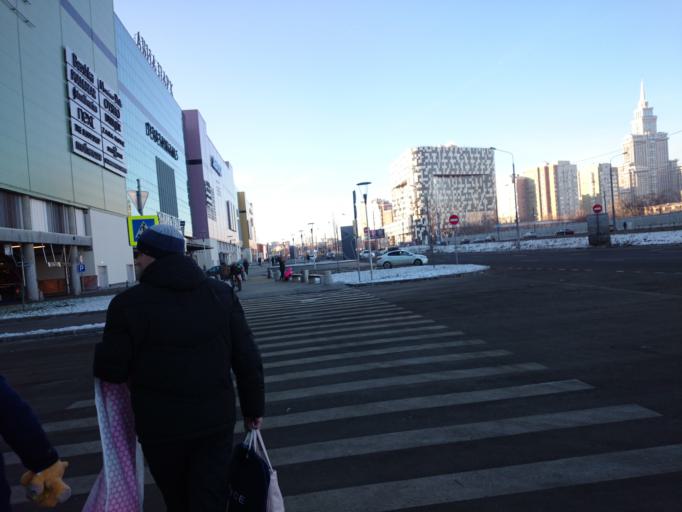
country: RU
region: Moscow
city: Sokol
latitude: 55.7909
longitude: 37.5331
